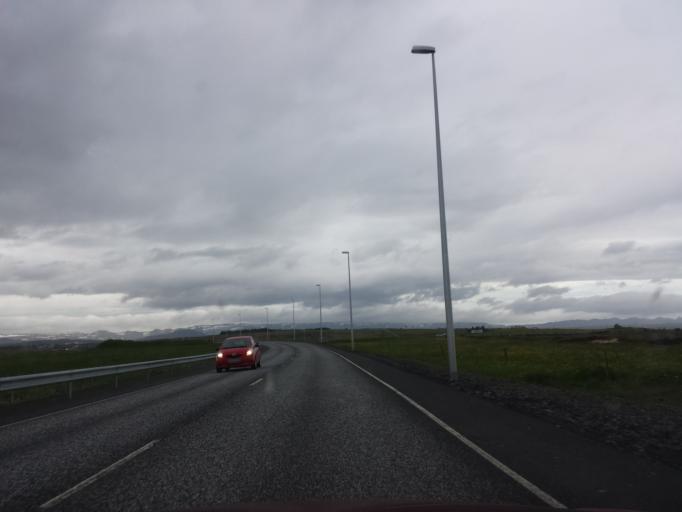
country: IS
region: Capital Region
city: Alftanes
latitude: 64.0992
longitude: -22.0067
